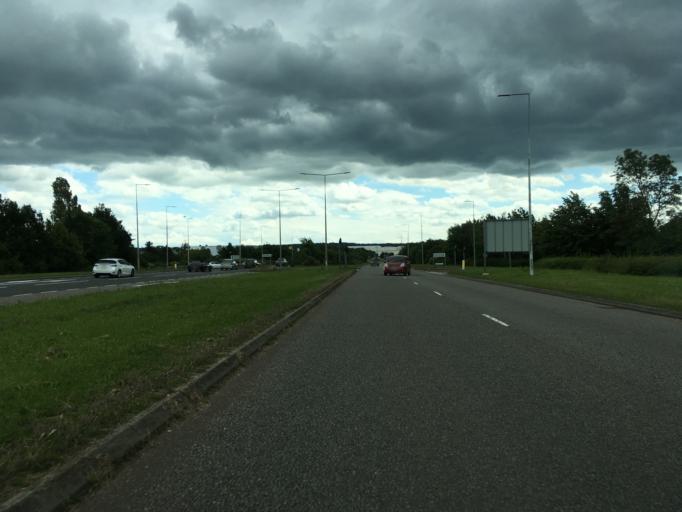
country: GB
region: England
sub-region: Milton Keynes
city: Broughton
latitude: 52.0390
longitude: -0.6931
